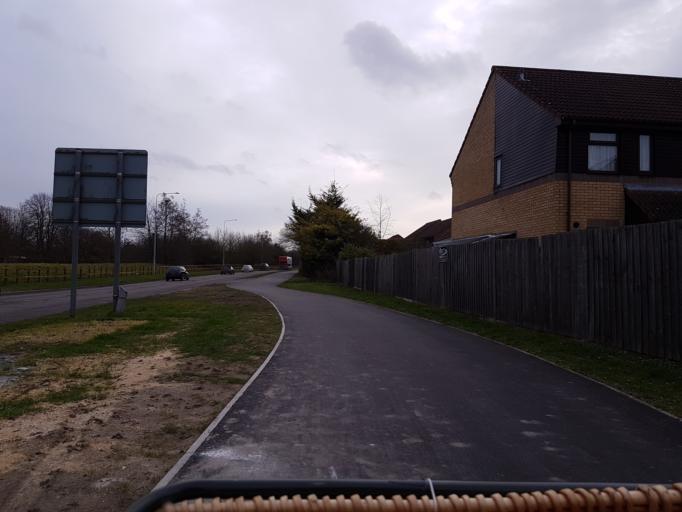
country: GB
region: England
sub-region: Cambridgeshire
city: Fulbourn
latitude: 52.1862
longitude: 0.1851
